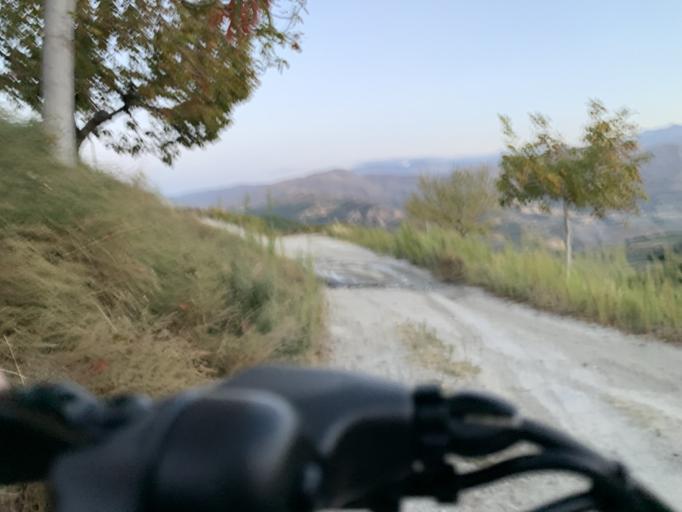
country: ES
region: Andalusia
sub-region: Provincia de Granada
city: Beas de Granada
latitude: 37.2221
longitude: -3.4584
